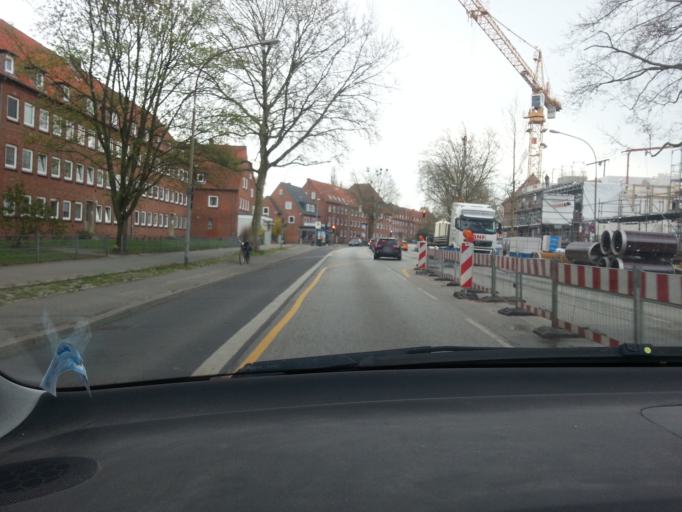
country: DE
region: Schleswig-Holstein
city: Luebeck
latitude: 53.8497
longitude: 10.7052
